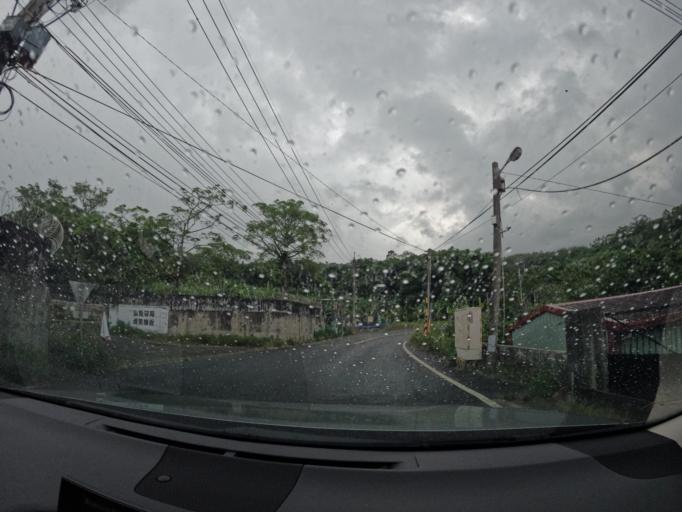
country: TW
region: Taiwan
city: Lugu
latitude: 23.8457
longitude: 120.7662
